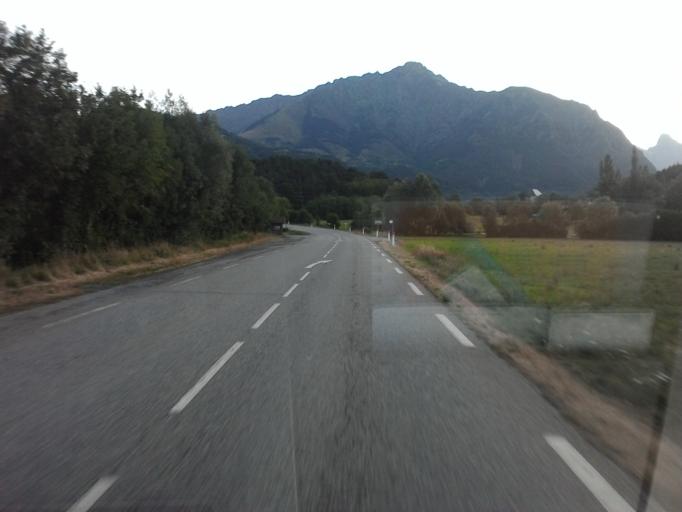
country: FR
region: Provence-Alpes-Cote d'Azur
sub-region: Departement des Hautes-Alpes
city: Saint-Bonnet-en-Champsaur
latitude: 44.7643
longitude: 6.0127
